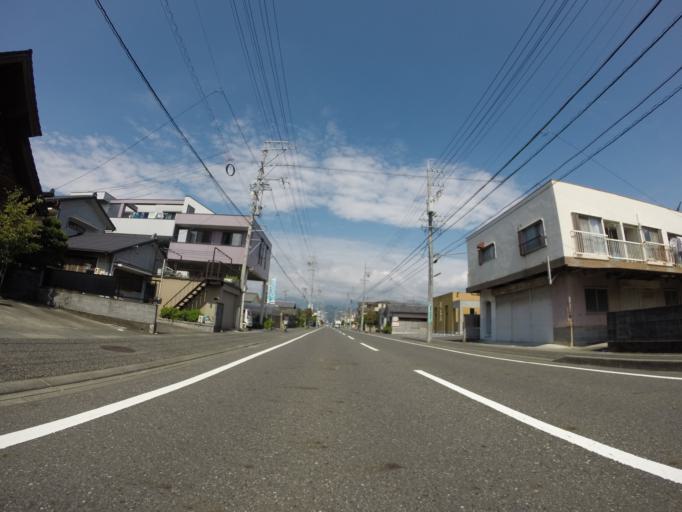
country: JP
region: Shizuoka
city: Shizuoka-shi
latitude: 35.0073
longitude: 138.4730
